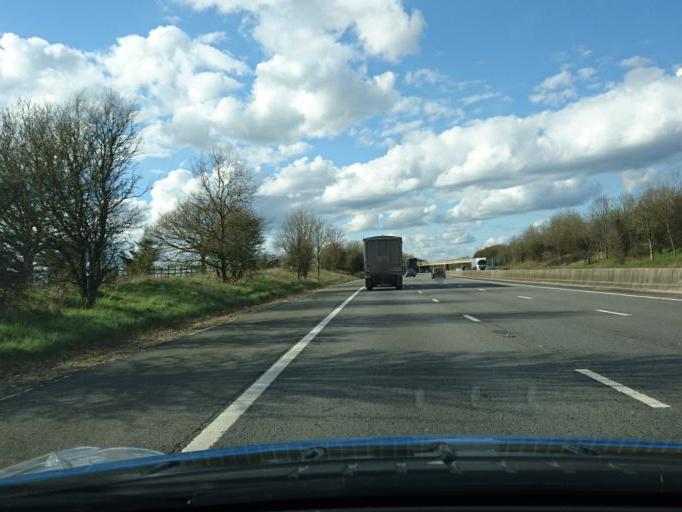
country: GB
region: England
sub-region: Wiltshire
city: Aldbourne
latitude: 51.4924
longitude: -1.5803
